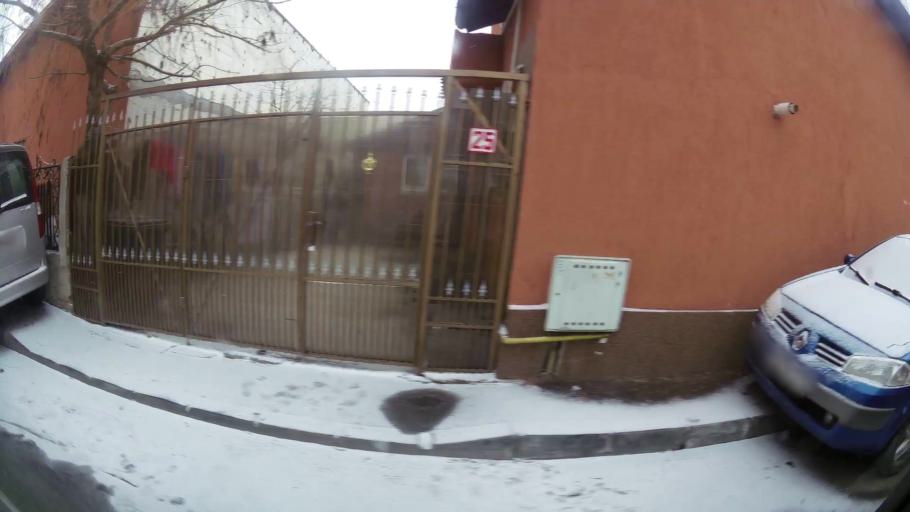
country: RO
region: Prahova
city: Ploiesti
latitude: 44.9534
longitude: 26.0150
